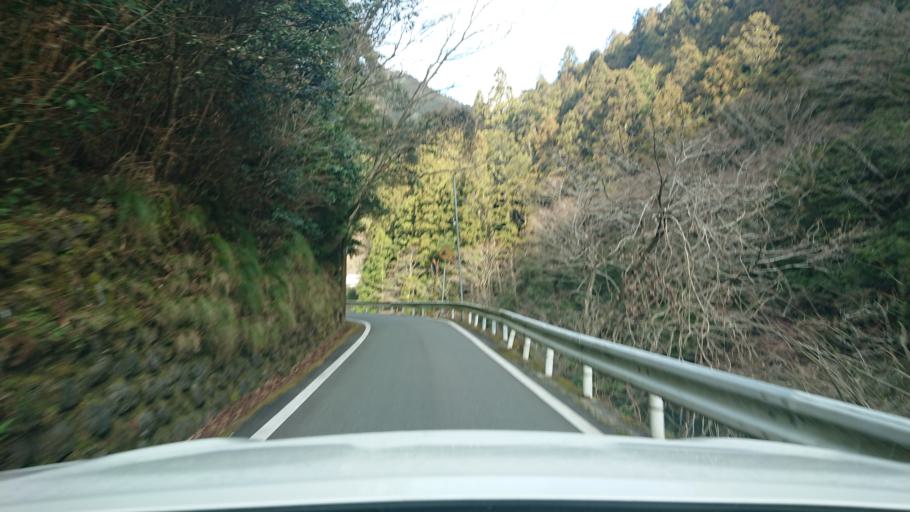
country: JP
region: Tokushima
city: Ishii
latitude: 33.8997
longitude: 134.3967
